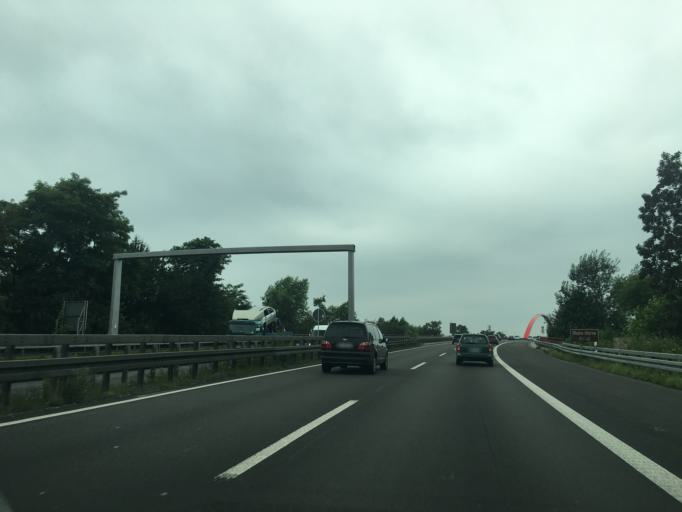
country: DE
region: North Rhine-Westphalia
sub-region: Regierungsbezirk Dusseldorf
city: Essen
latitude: 51.5034
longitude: 6.9828
